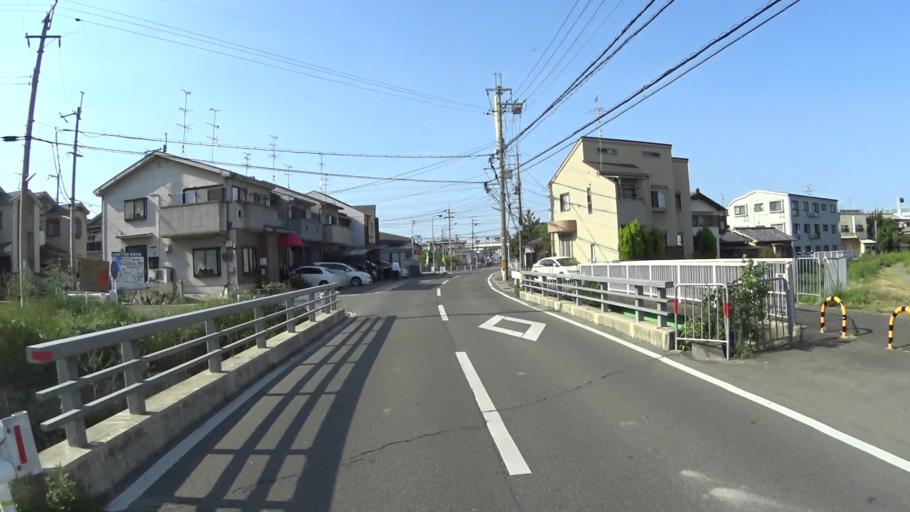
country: JP
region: Kyoto
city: Yawata
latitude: 34.9074
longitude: 135.6887
